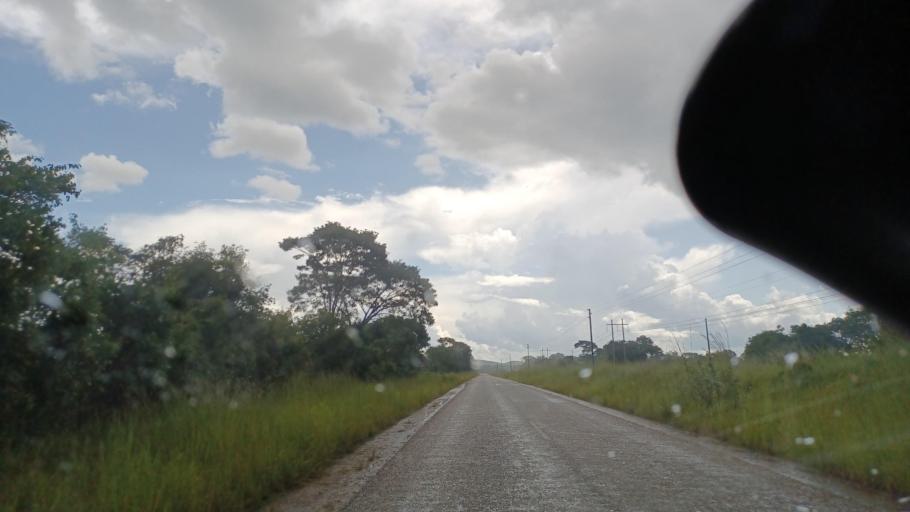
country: ZM
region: North-Western
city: Kasempa
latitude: -13.1016
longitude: 25.8911
